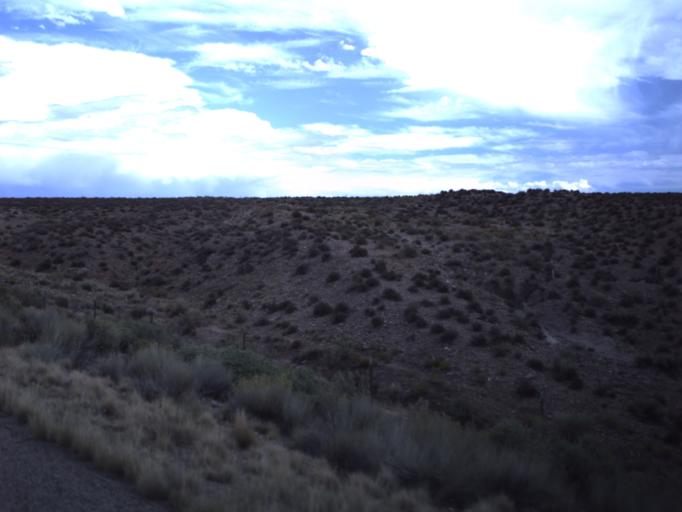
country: US
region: Utah
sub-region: San Juan County
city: Blanding
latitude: 37.2799
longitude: -109.3695
